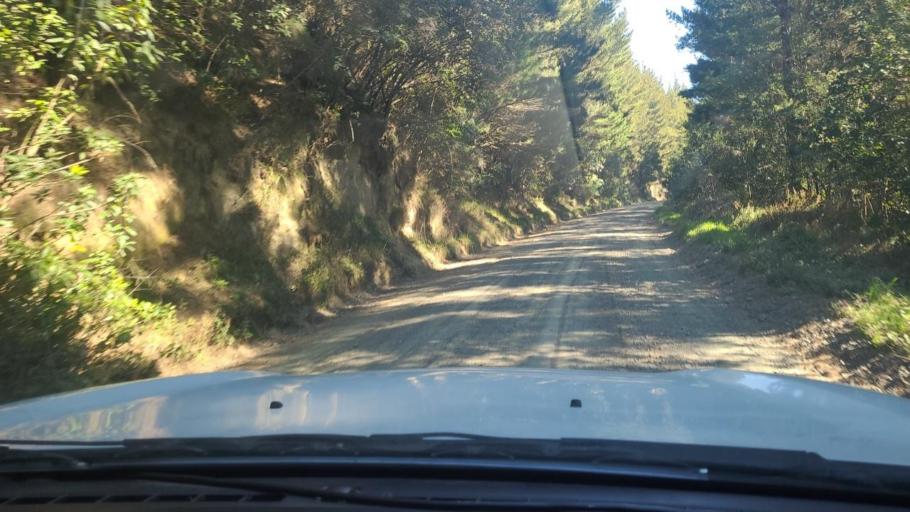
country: NZ
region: Hawke's Bay
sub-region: Napier City
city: Taradale
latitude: -39.4079
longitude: 176.4768
